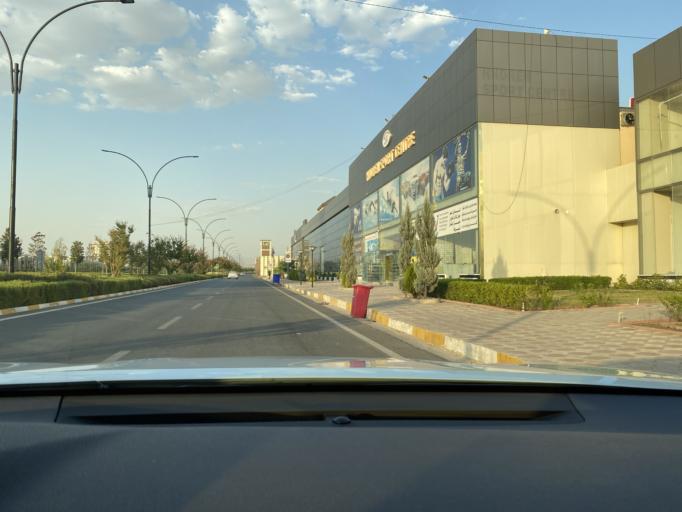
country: IQ
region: Arbil
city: Erbil
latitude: 36.2177
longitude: 43.9973
